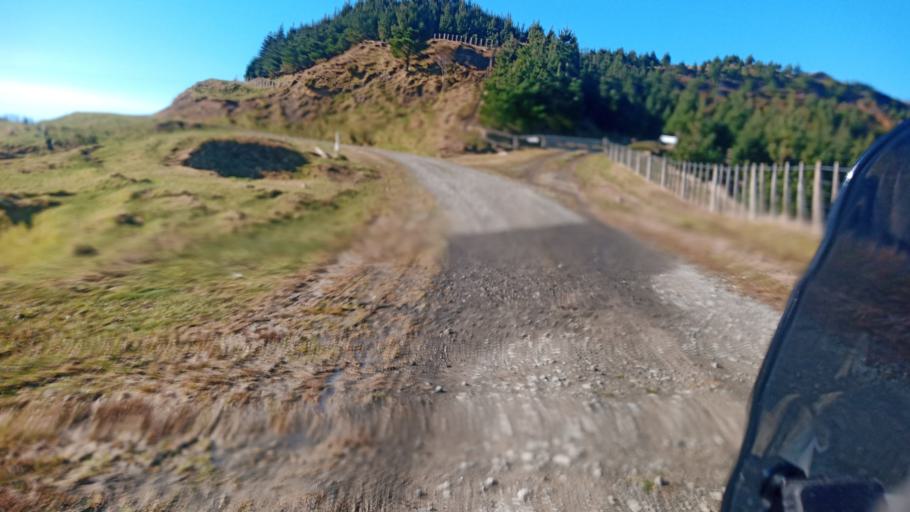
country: NZ
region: Gisborne
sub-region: Gisborne District
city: Gisborne
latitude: -38.1508
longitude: 177.8839
